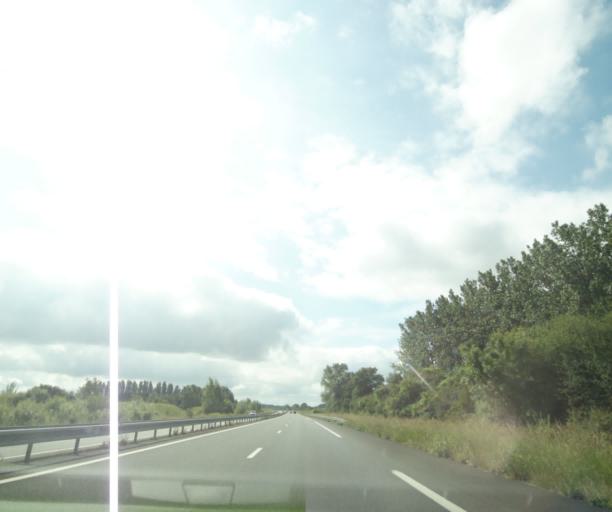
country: FR
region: Pays de la Loire
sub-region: Departement de Maine-et-Loire
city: Vivy
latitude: 47.3507
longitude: -0.0749
